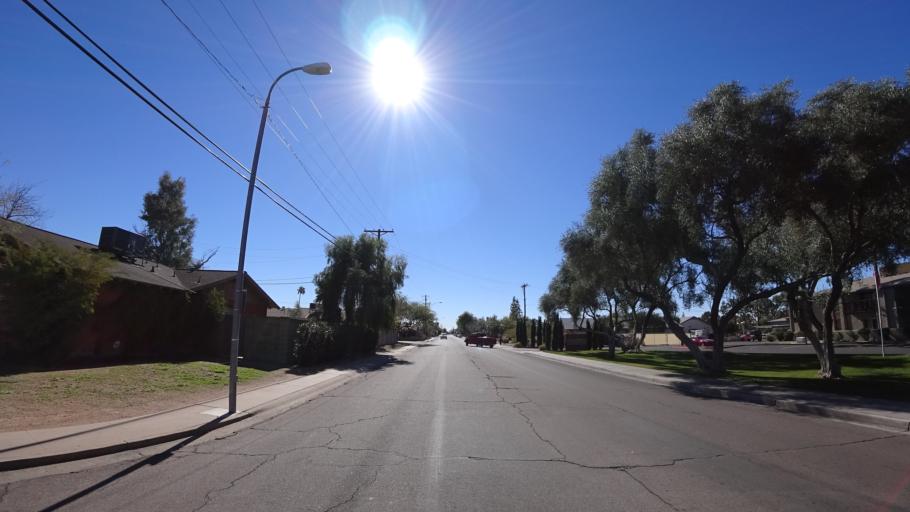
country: US
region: Arizona
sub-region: Maricopa County
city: Scottsdale
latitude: 33.4998
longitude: -111.9046
